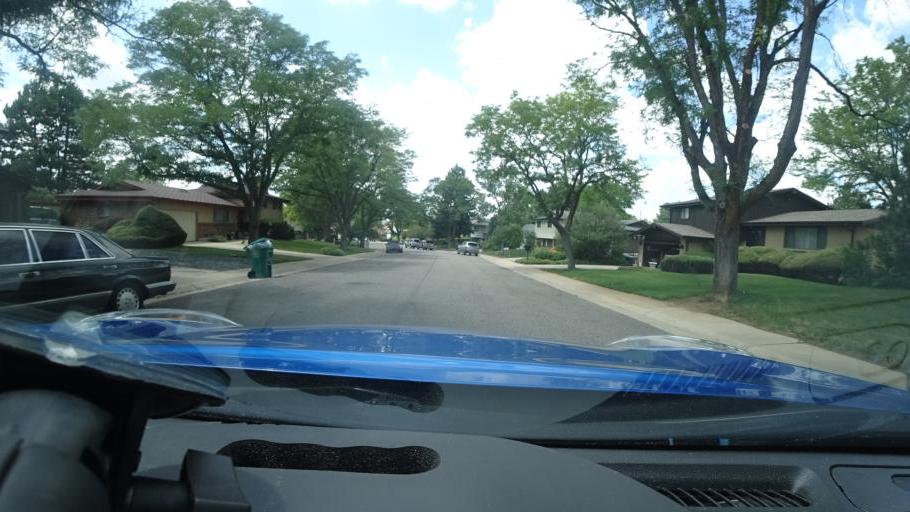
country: US
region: Colorado
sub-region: Adams County
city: Aurora
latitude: 39.7034
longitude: -104.8368
